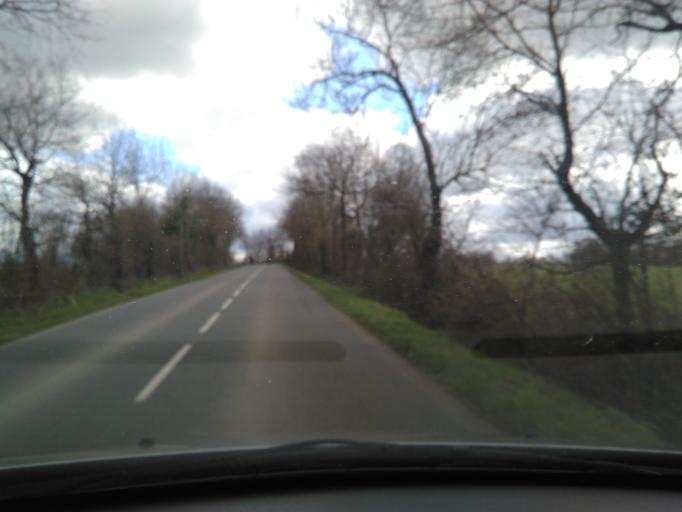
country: FR
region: Pays de la Loire
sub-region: Departement de la Vendee
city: Saint-Martin-des-Noyers
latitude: 46.7069
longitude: -1.1515
